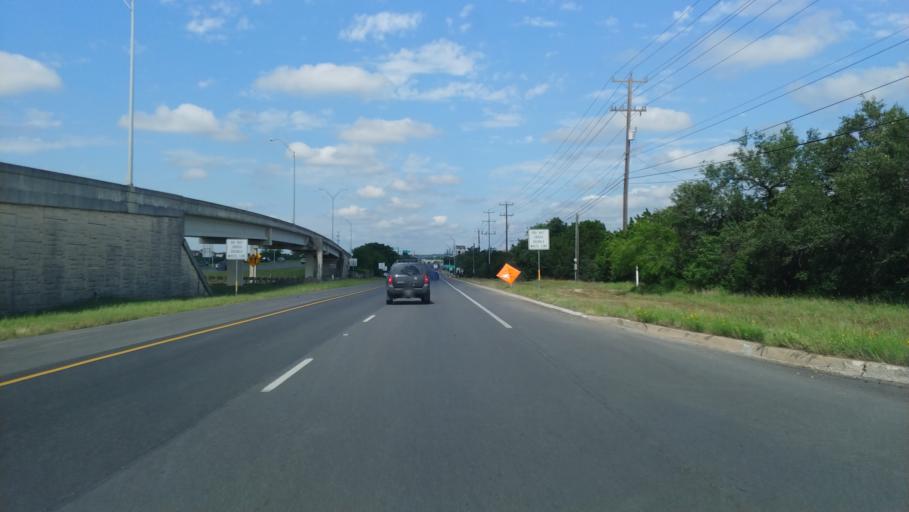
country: US
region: Texas
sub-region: Bexar County
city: Shavano Park
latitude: 29.5894
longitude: -98.6144
